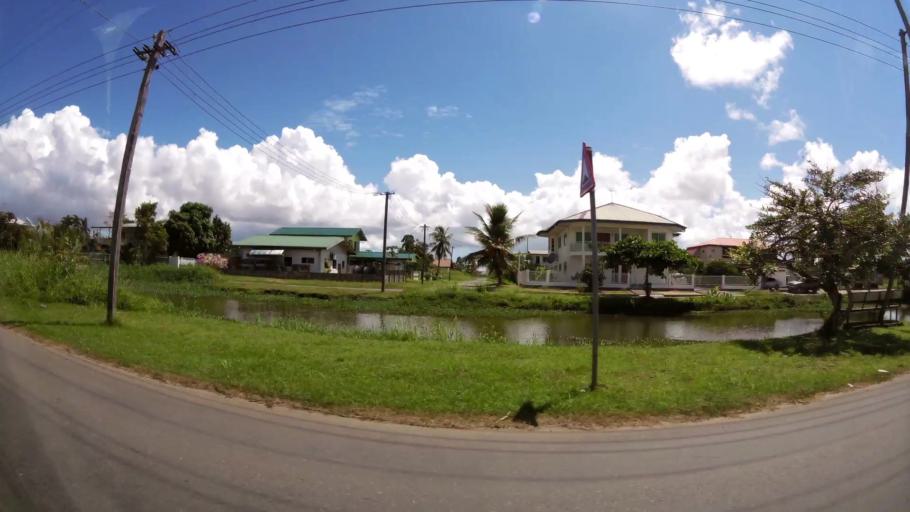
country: SR
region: Paramaribo
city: Paramaribo
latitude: 5.8616
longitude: -55.1334
